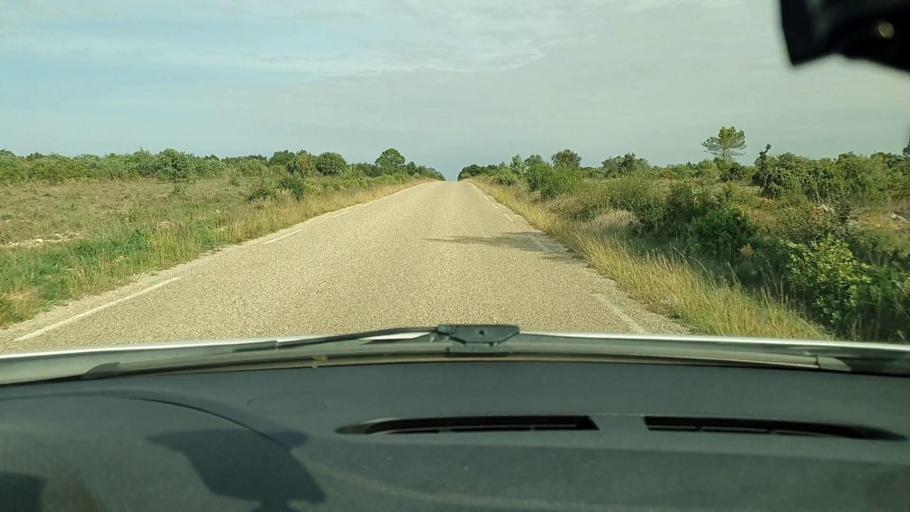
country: FR
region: Languedoc-Roussillon
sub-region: Departement du Gard
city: Saint-Quentin-la-Poterie
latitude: 44.1215
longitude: 4.4117
